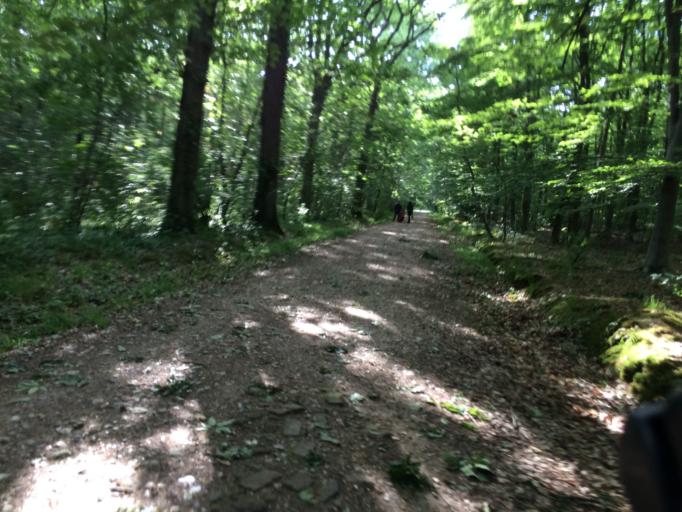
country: FR
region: Ile-de-France
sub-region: Departement de l'Essonne
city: Igny
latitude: 48.7507
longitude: 2.2445
